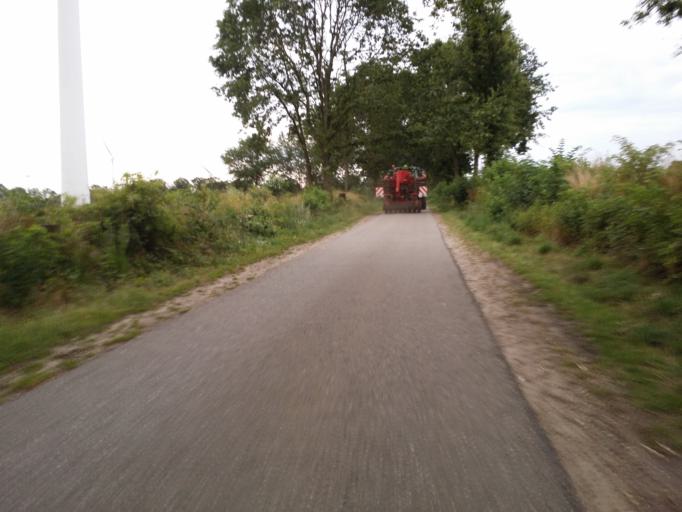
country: DE
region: Schleswig-Holstein
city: Kleve
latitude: 53.9840
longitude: 9.4070
